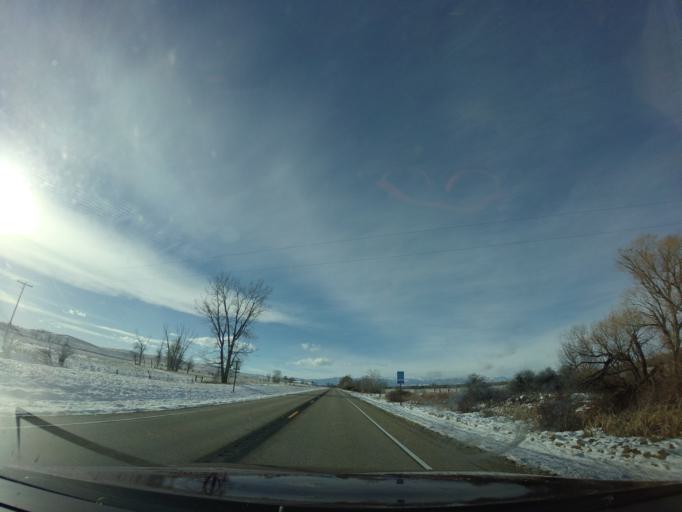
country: US
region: Montana
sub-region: Stillwater County
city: Columbus
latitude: 45.4147
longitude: -109.1148
